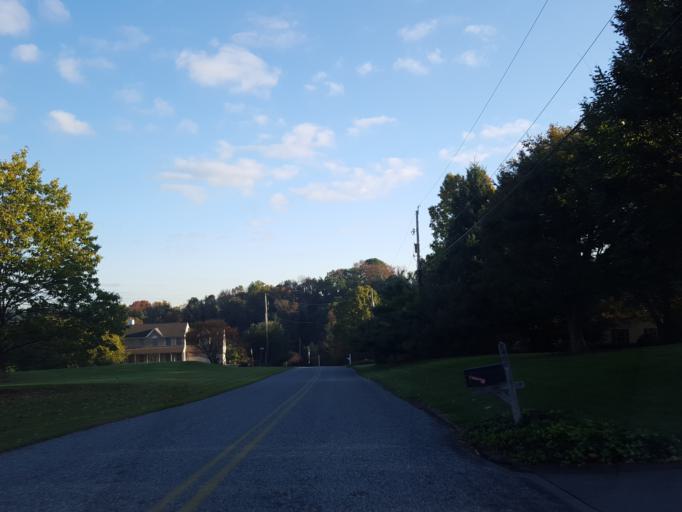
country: US
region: Pennsylvania
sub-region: York County
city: Yoe
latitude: 39.9395
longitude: -76.6331
